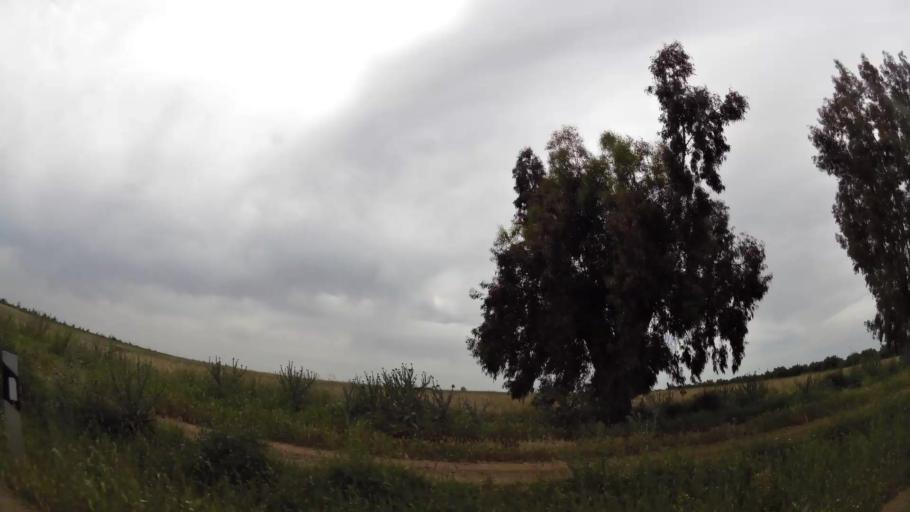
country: MA
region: Rabat-Sale-Zemmour-Zaer
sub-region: Khemisset
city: Tiflet
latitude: 33.8120
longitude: -6.2726
